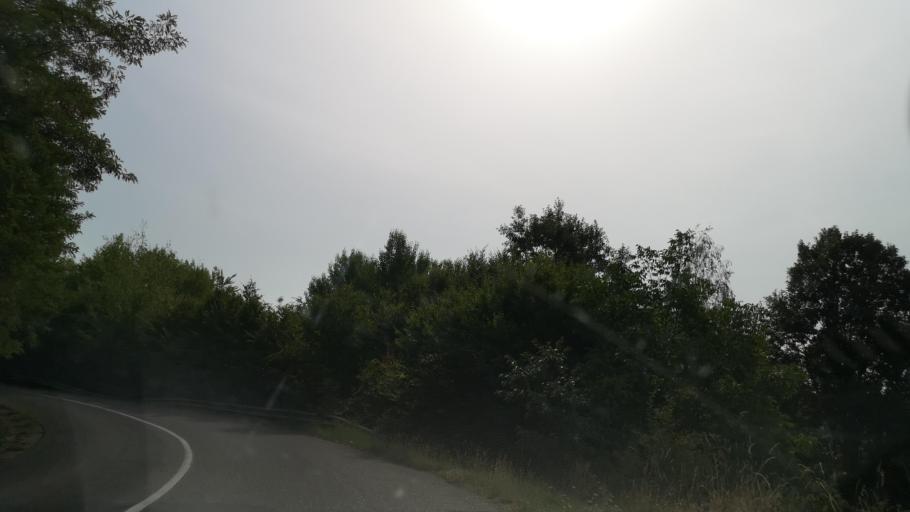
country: SK
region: Banskobystricky
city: Revuca
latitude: 48.5857
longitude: 20.0545
